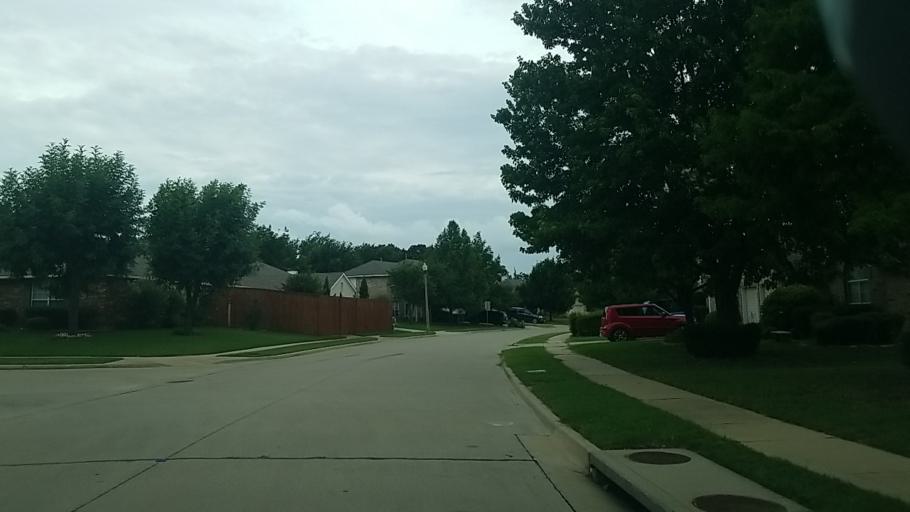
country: US
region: Texas
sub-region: Denton County
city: Corinth
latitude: 33.1669
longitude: -97.1073
